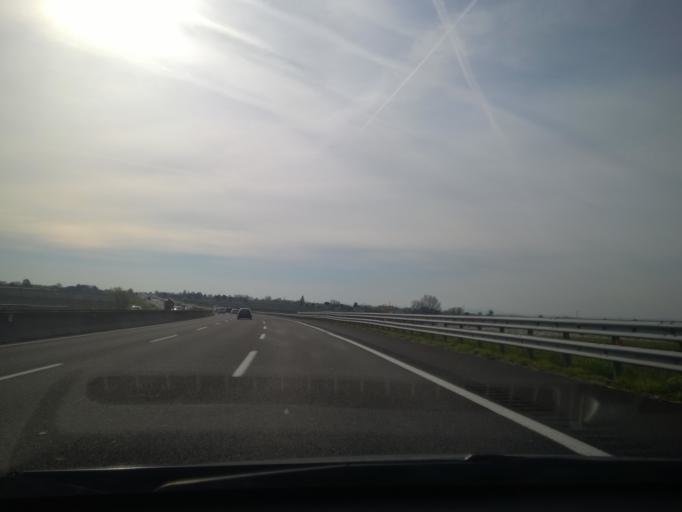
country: IT
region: Emilia-Romagna
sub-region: Provincia di Ravenna
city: Granarolo
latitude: 44.3124
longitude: 11.9290
